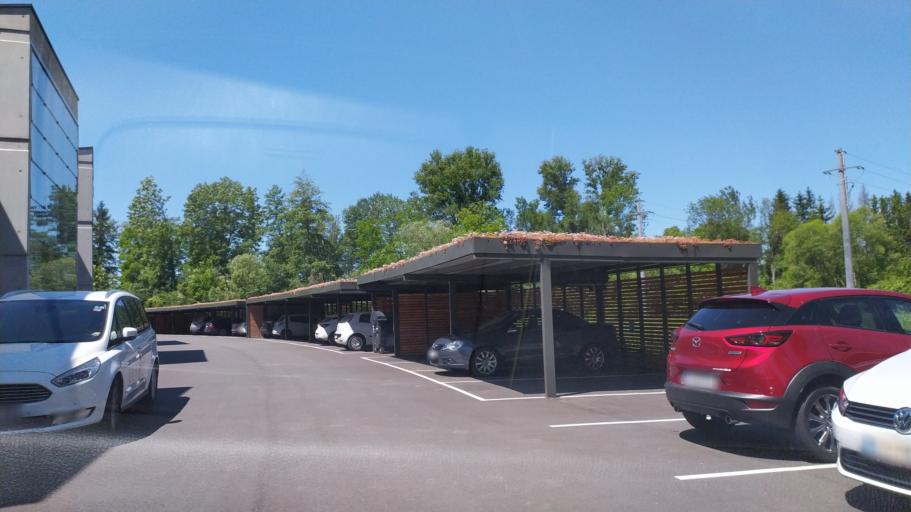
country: AT
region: Upper Austria
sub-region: Politischer Bezirk Linz-Land
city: Ansfelden
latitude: 48.2329
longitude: 14.2766
